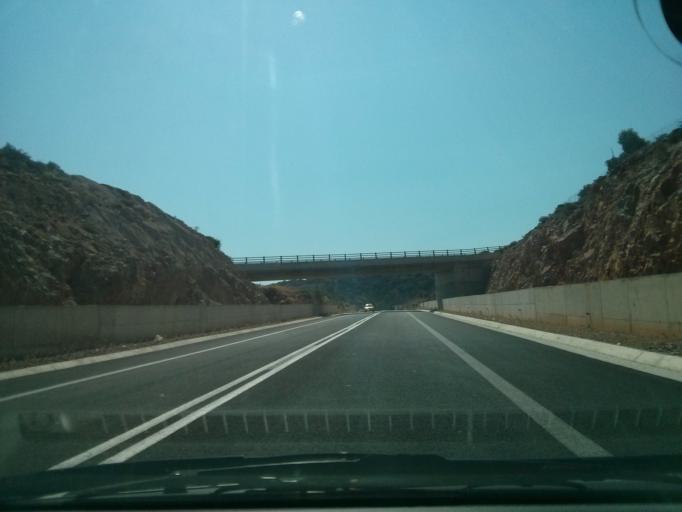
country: GR
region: Crete
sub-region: Nomos Lasithiou
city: Agios Nikolaos
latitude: 35.1650
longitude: 25.7042
